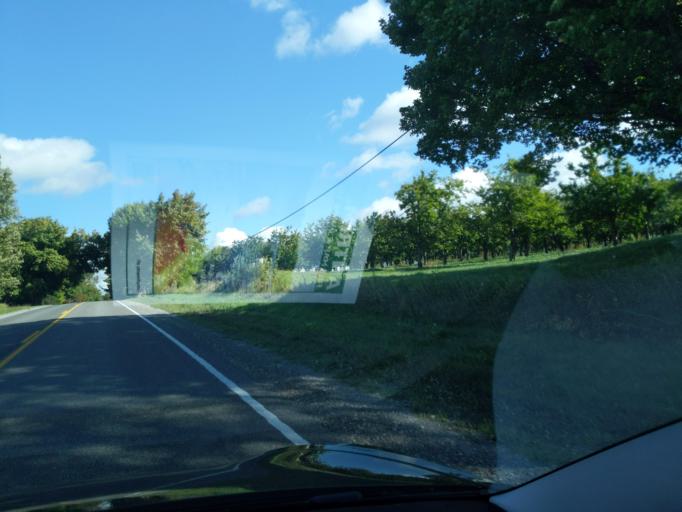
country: US
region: Michigan
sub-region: Antrim County
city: Elk Rapids
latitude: 44.9404
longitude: -85.3575
